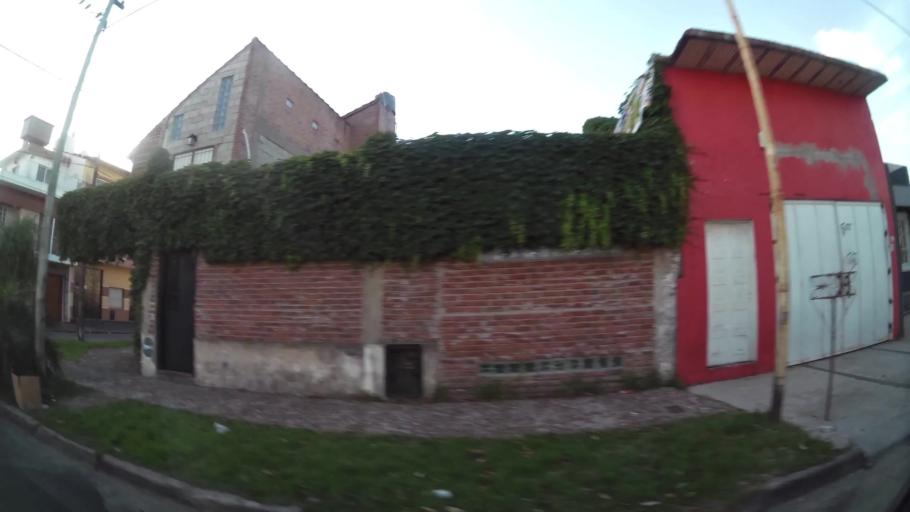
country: AR
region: Buenos Aires F.D.
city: Villa Lugano
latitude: -34.6928
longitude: -58.4875
